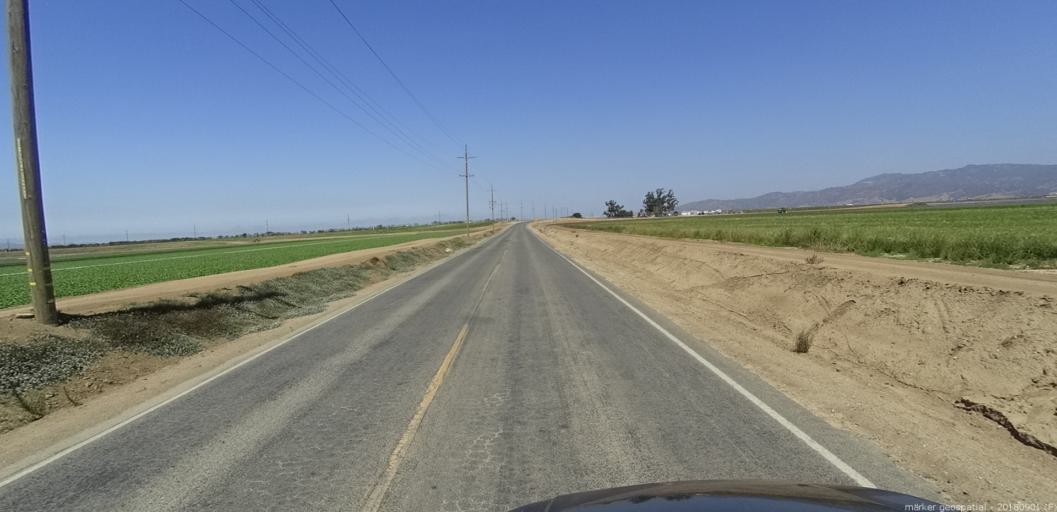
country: US
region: California
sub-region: Monterey County
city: Chualar
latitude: 36.5782
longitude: -121.4956
